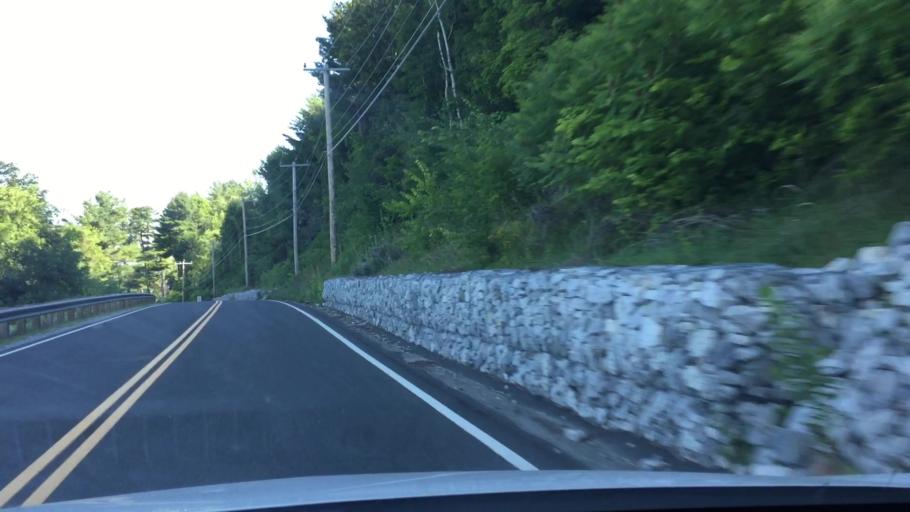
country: US
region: Massachusetts
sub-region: Berkshire County
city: Lee
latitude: 42.2719
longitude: -73.2367
